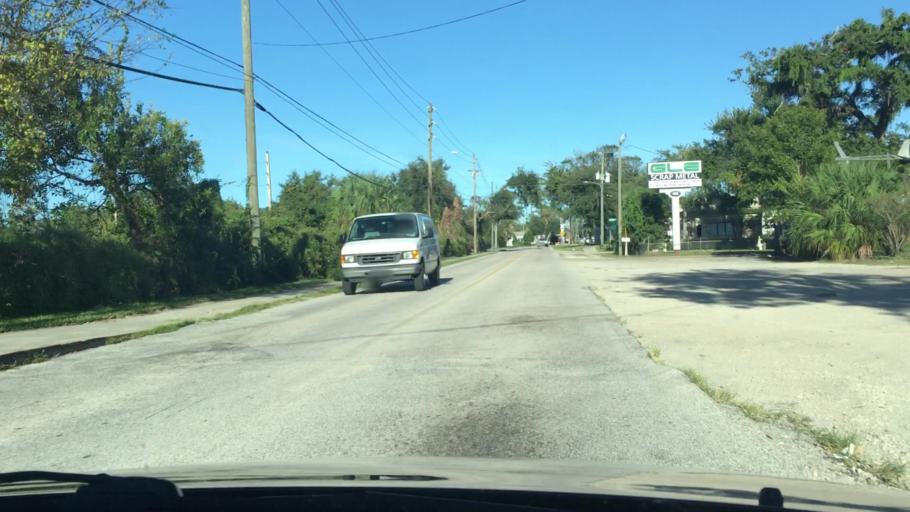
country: US
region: Florida
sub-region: Volusia County
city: Holly Hill
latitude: 29.2537
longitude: -81.0517
